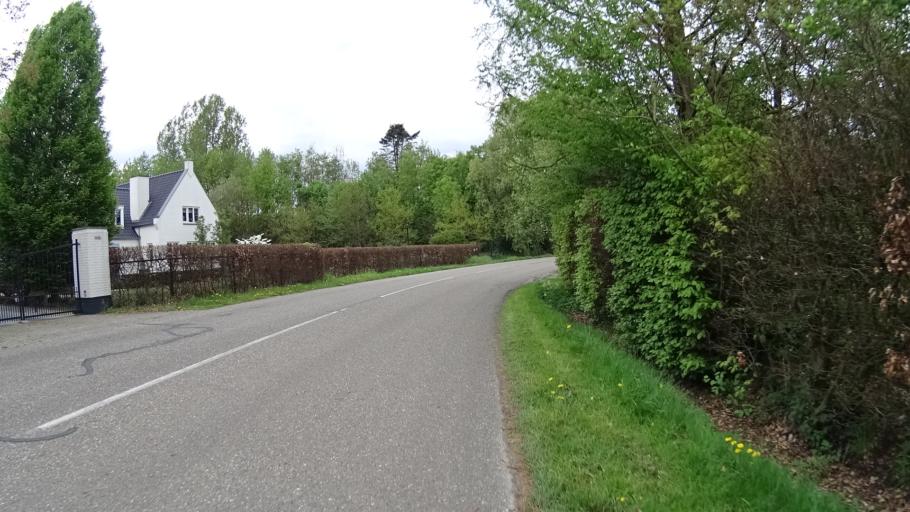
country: NL
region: North Brabant
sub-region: Gemeente Nuenen, Gerwen en Nederwetten
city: Nuenen
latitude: 51.5118
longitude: 5.5799
